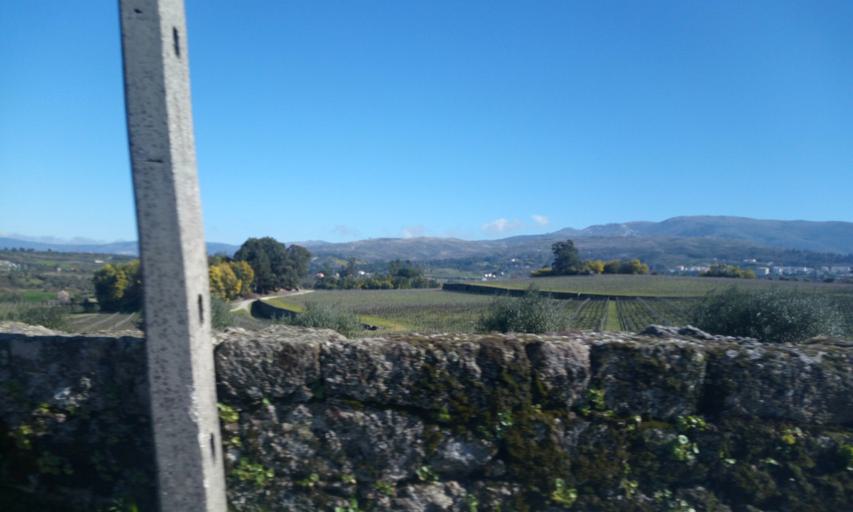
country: PT
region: Guarda
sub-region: Manteigas
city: Manteigas
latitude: 40.5105
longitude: -7.6082
